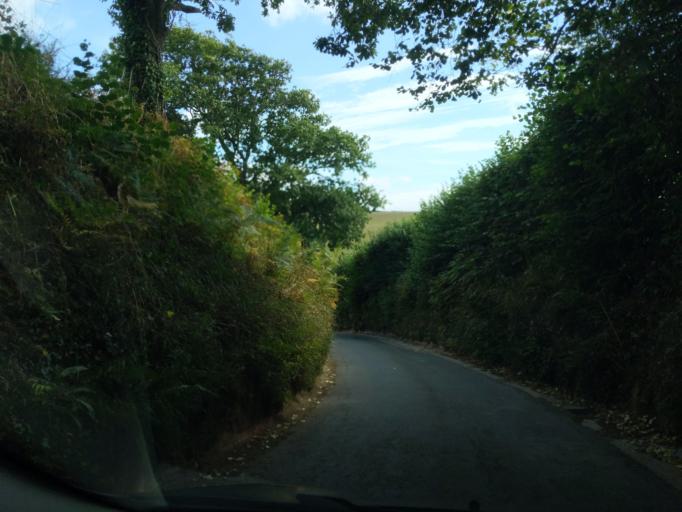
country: GB
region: England
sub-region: Devon
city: Modbury
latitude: 50.3598
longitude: -3.8952
